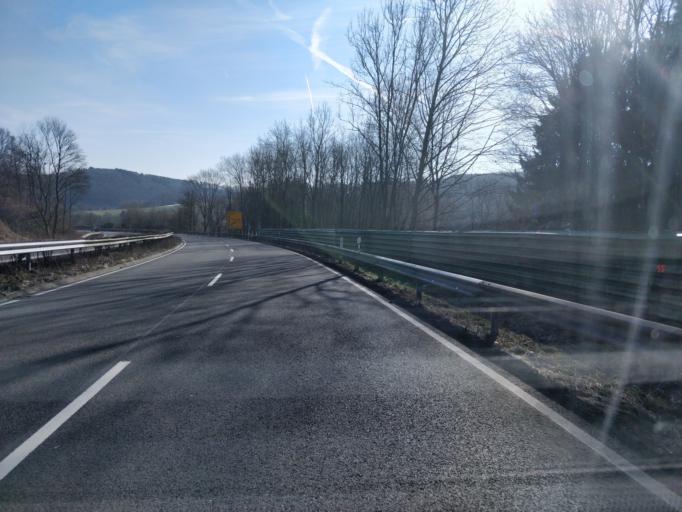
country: DE
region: North Rhine-Westphalia
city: Wiehl
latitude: 50.9633
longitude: 7.5170
